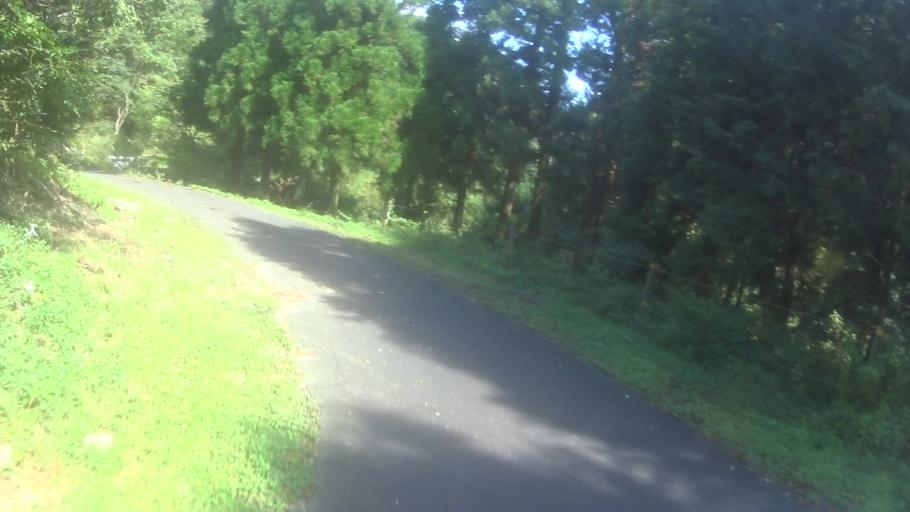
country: JP
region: Kyoto
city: Miyazu
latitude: 35.6717
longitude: 135.1431
